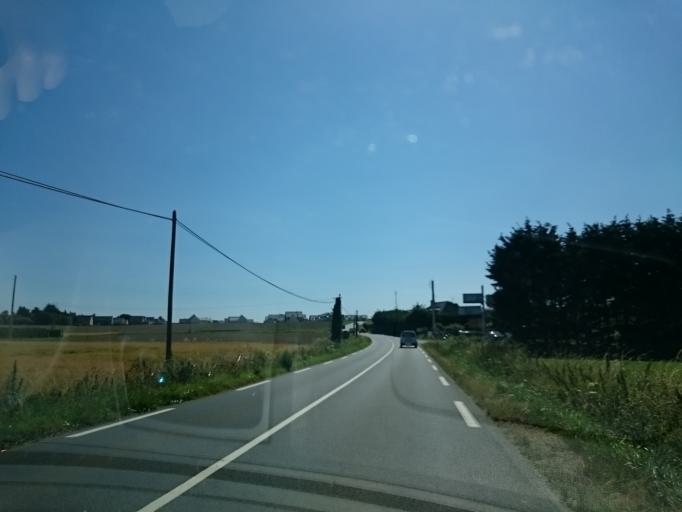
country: FR
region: Brittany
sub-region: Departement d'Ille-et-Vilaine
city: Saint-Coulomb
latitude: 48.6629
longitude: -1.9600
